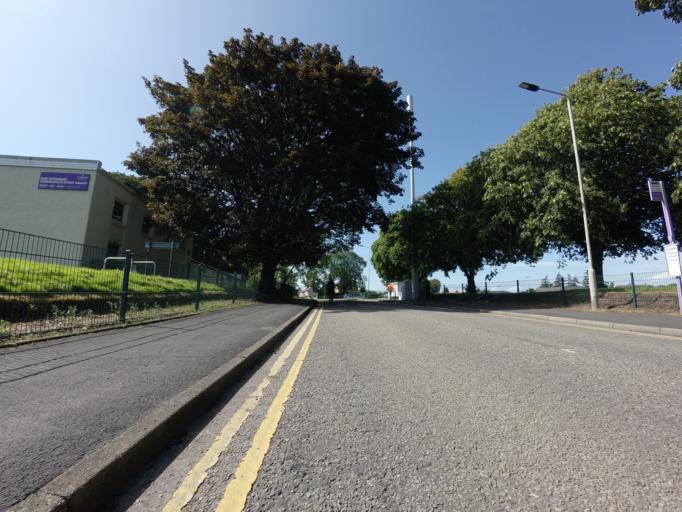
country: GB
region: Scotland
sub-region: Highland
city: Inverness
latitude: 57.4738
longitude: -4.2097
